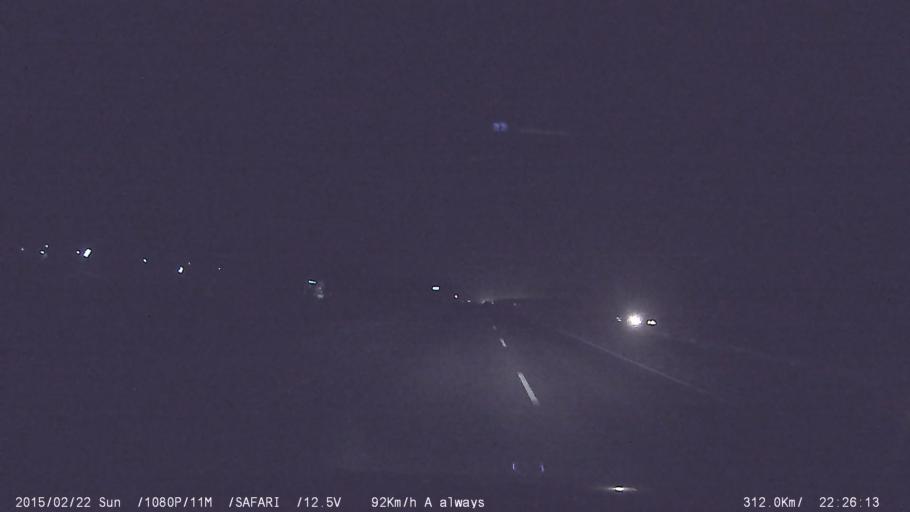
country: IN
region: Tamil Nadu
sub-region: Namakkal
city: Velur
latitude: 11.0534
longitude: 78.0463
